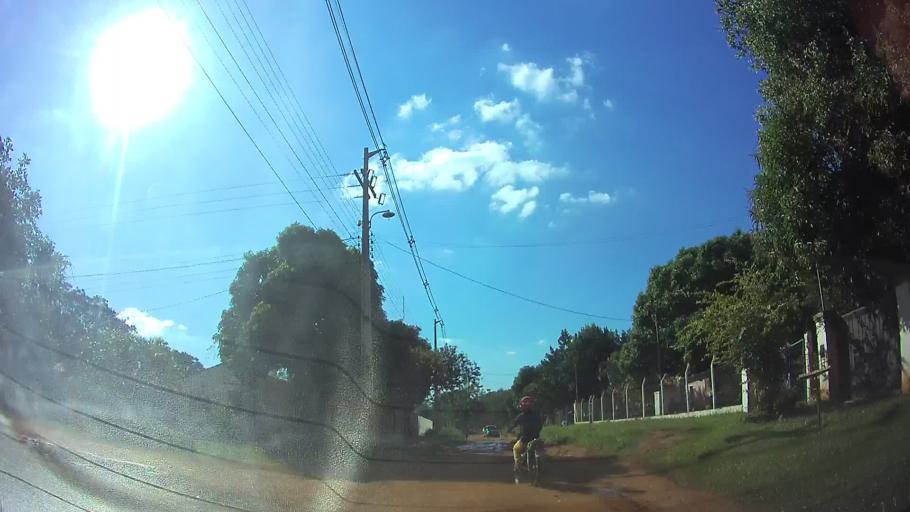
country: PY
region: Central
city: Limpio
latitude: -25.2486
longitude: -57.4747
